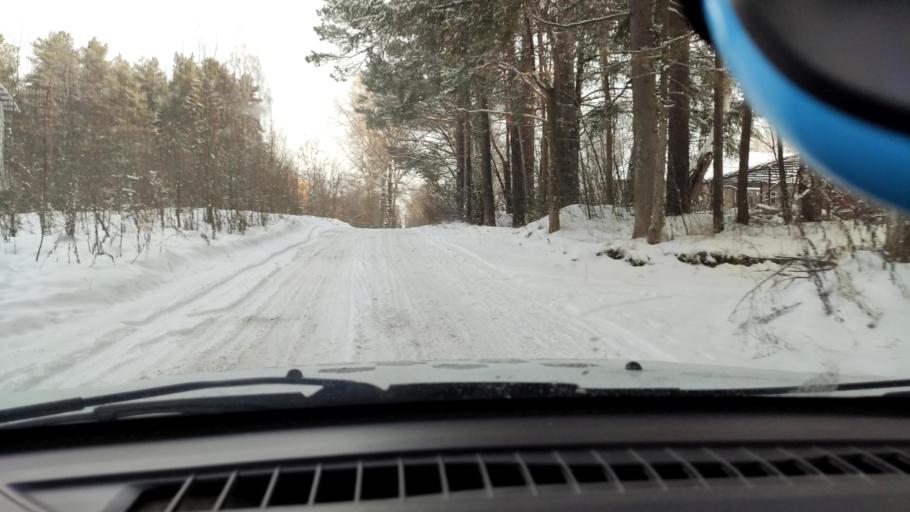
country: RU
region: Perm
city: Perm
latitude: 58.0967
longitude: 56.2890
